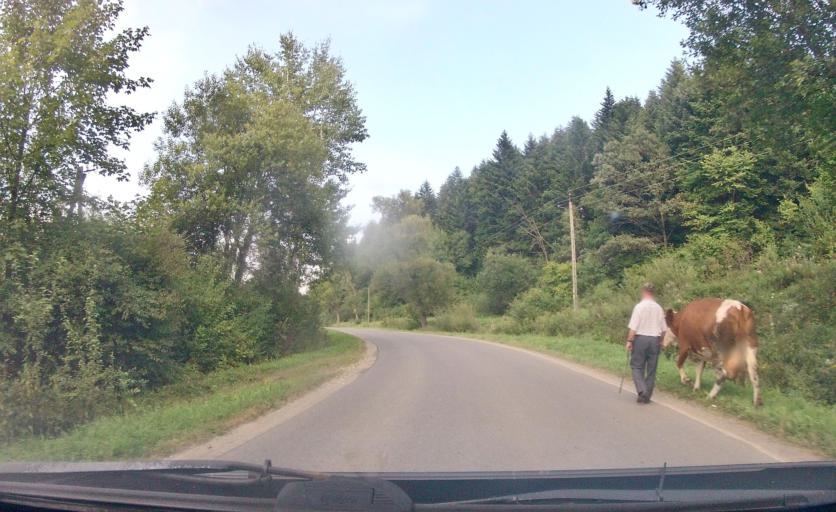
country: PL
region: Subcarpathian Voivodeship
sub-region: Powiat krosnienski
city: Dukla
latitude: 49.5429
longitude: 21.6195
